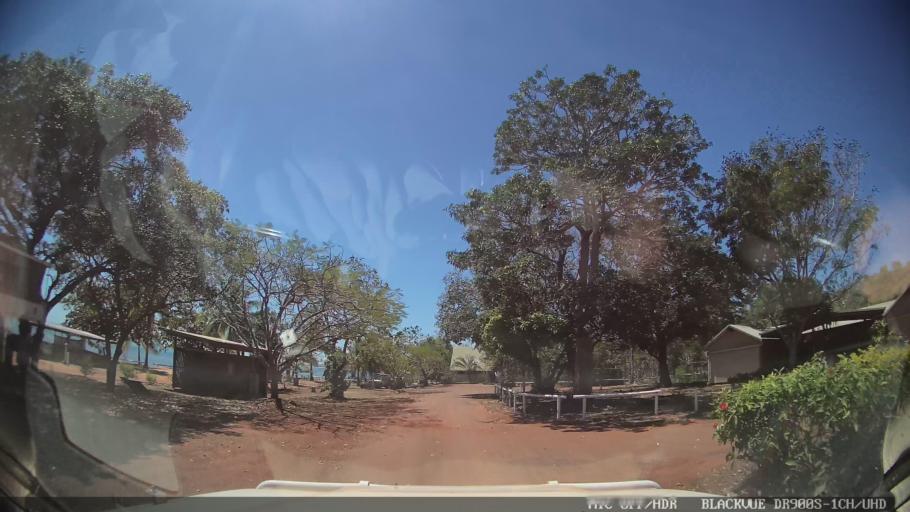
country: AU
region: Queensland
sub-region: Torres
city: Thursday Island
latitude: -10.8459
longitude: 142.3691
